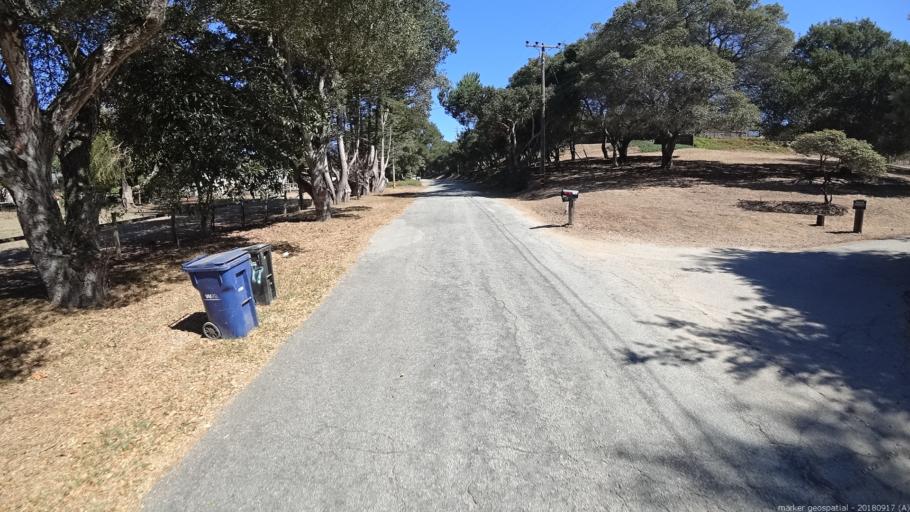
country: US
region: California
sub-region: San Benito County
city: Aromas
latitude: 36.8311
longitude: -121.6495
